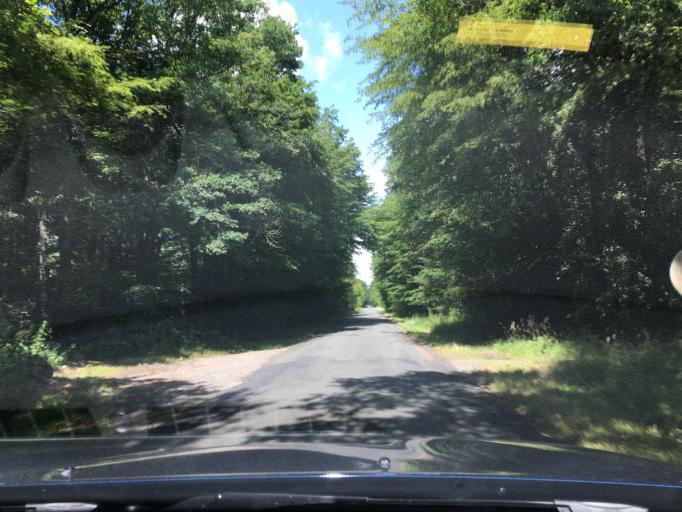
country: FR
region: Centre
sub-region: Departement du Loiret
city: Chanteau
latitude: 48.0044
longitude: 1.9333
